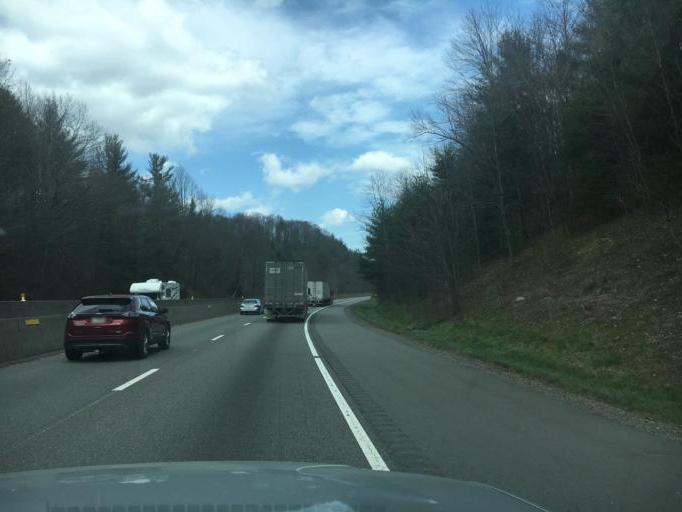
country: US
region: North Carolina
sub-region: Haywood County
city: Cove Creek
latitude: 35.6159
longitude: -83.0119
